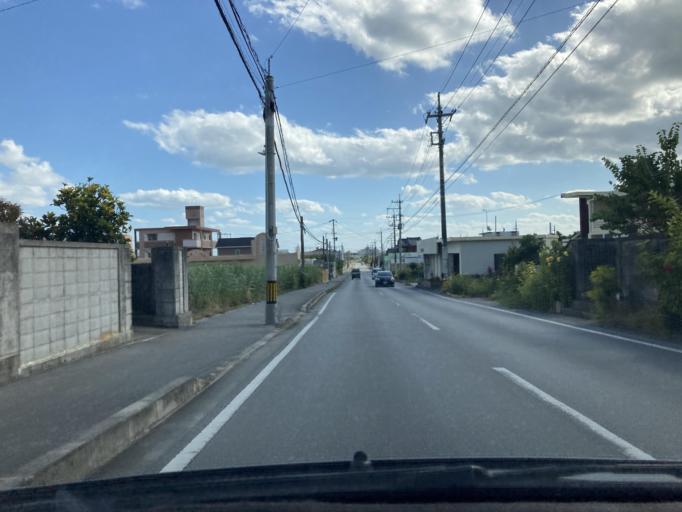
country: JP
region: Okinawa
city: Gushikawa
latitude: 26.3485
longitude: 127.8463
